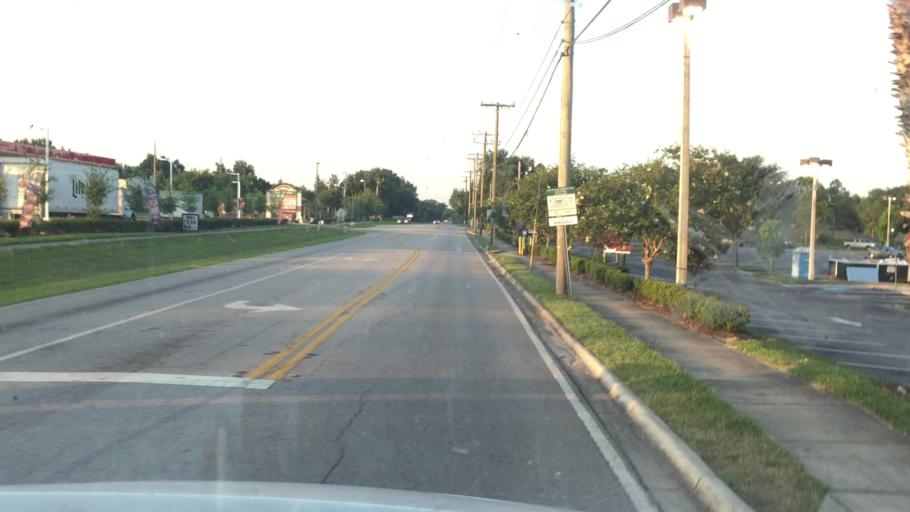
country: US
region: Florida
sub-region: Hillsborough County
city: Brandon
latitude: 27.9596
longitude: -82.2777
